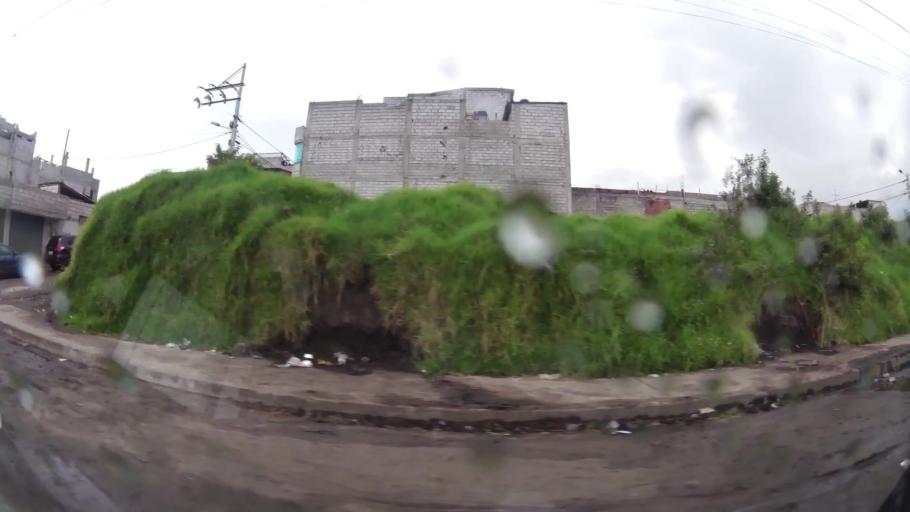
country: EC
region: Pichincha
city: Sangolqui
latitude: -0.3214
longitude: -78.5450
